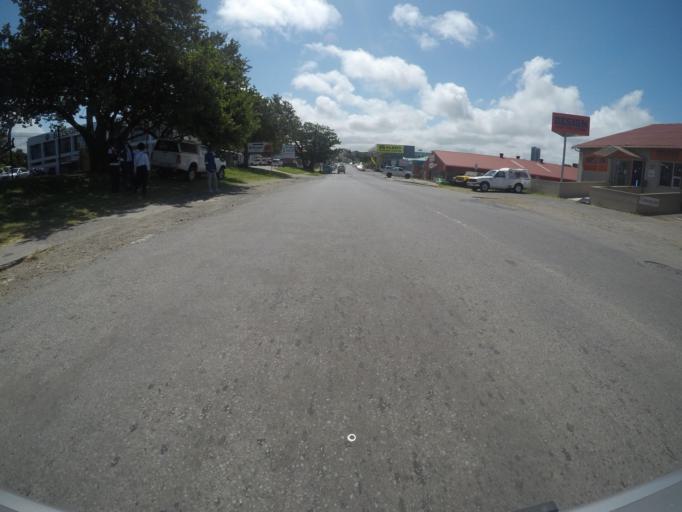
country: ZA
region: Eastern Cape
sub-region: Buffalo City Metropolitan Municipality
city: East London
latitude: -33.0059
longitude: 27.9093
